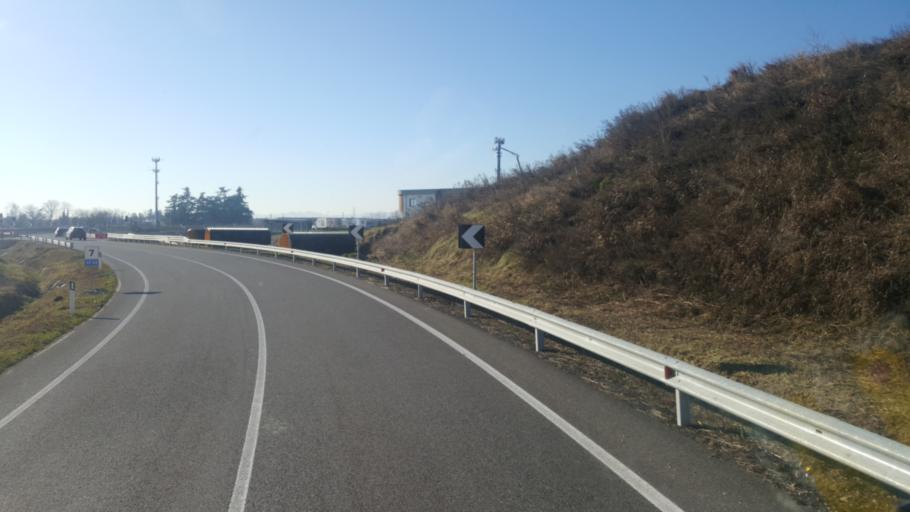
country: IT
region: Veneto
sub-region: Provincia di Vicenza
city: Breganze
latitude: 45.6956
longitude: 11.5697
